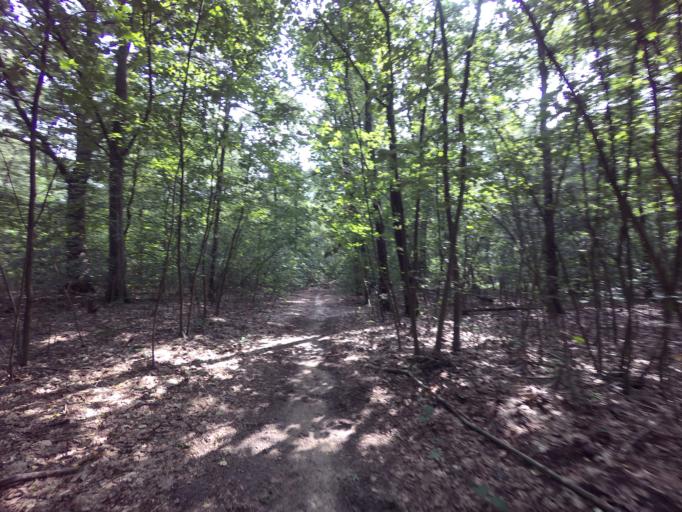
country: NL
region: Gelderland
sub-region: Gemeente Ede
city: Lunteren
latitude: 52.0802
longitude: 5.6538
